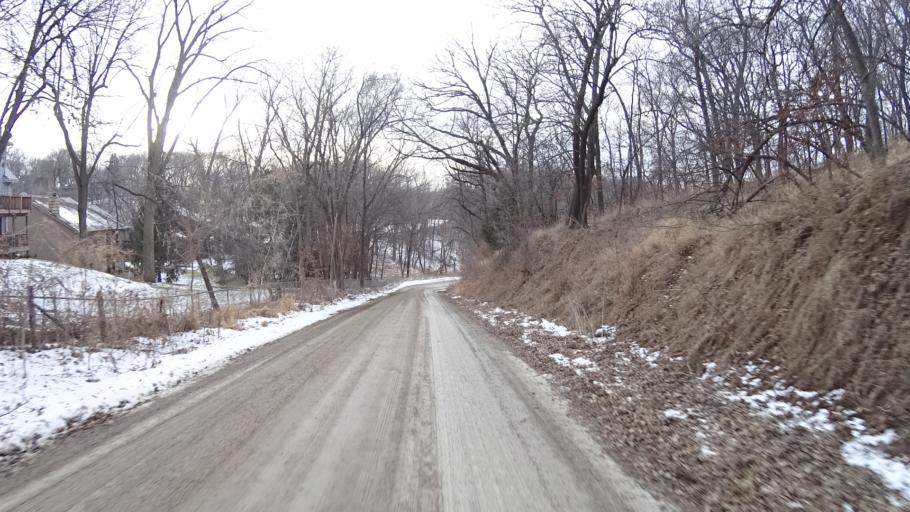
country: US
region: Nebraska
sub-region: Sarpy County
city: Bellevue
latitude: 41.1695
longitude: -95.9022
